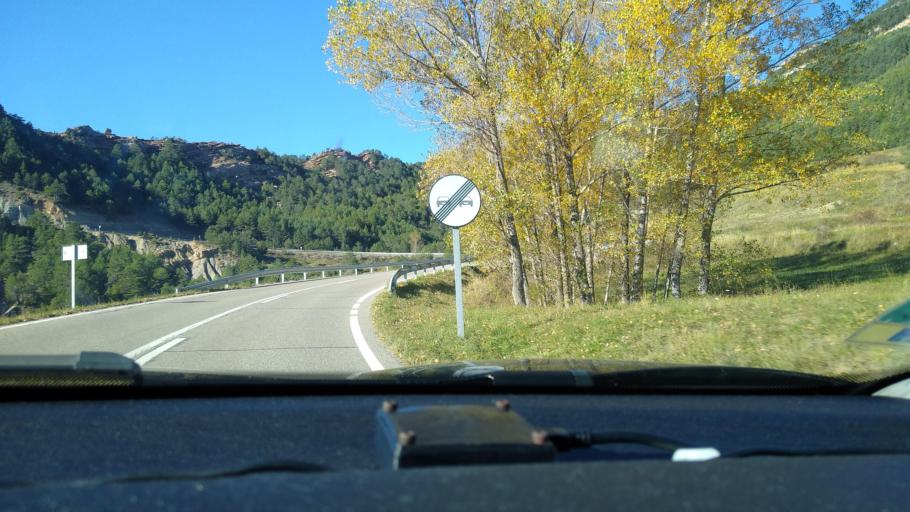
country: ES
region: Catalonia
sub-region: Provincia de Barcelona
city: Saldes
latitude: 42.2214
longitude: 1.7213
